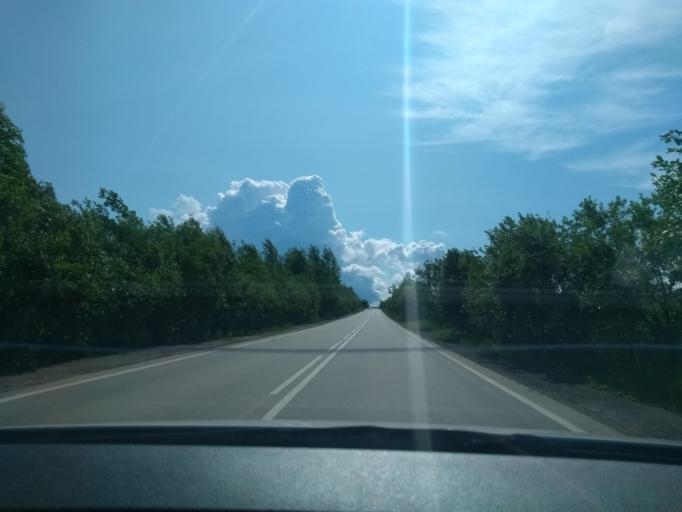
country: RU
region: Perm
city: Bershet'
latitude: 57.8166
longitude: 56.4441
